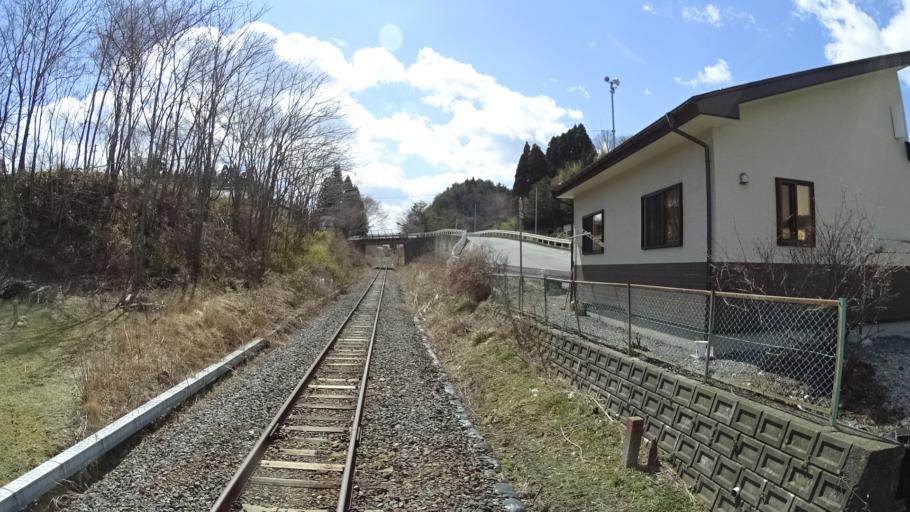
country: JP
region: Iwate
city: Yamada
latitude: 39.4302
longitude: 141.9736
